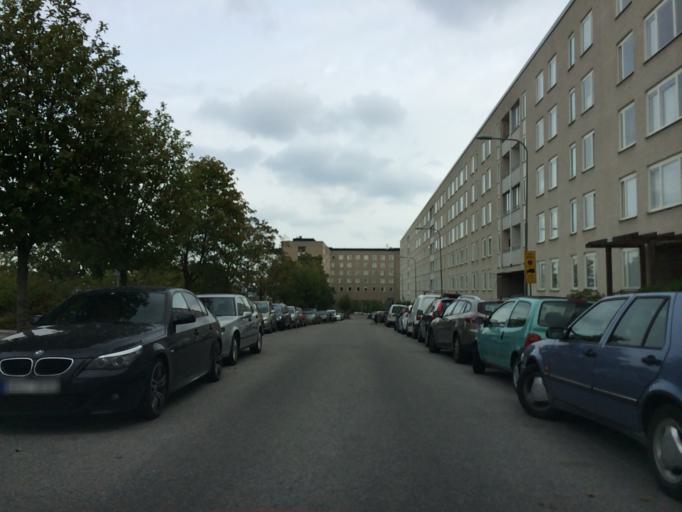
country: SE
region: Stockholm
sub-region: Stockholms Kommun
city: Arsta
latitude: 59.3083
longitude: 18.0128
